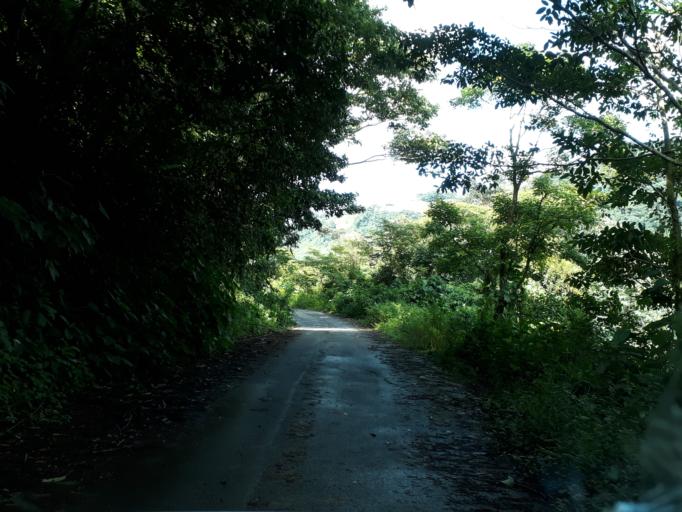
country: CO
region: Boyaca
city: Santa Maria
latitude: 4.7379
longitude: -73.3447
